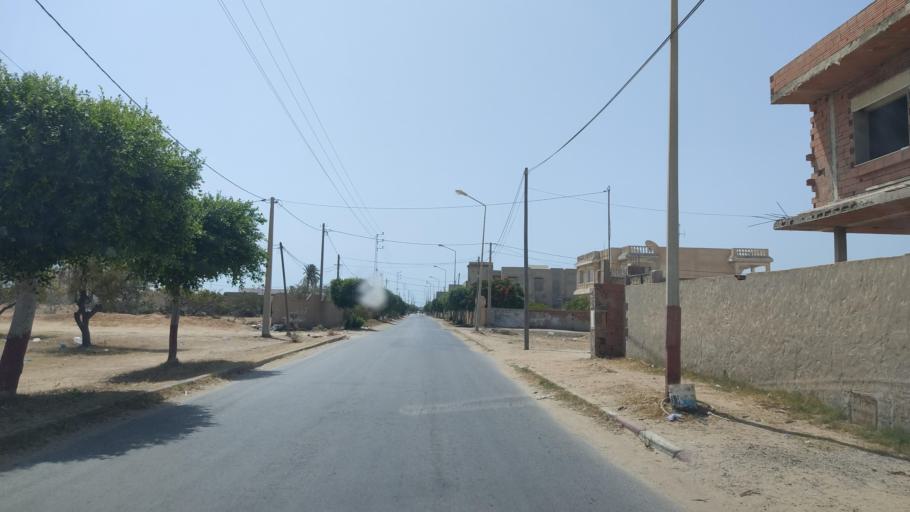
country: TN
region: Safaqis
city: Sfax
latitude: 34.6744
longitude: 10.7012
